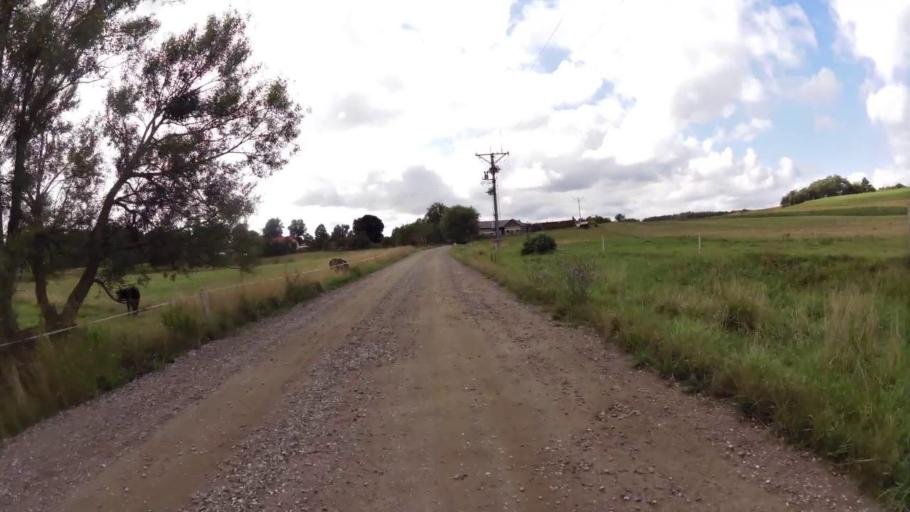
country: PL
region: West Pomeranian Voivodeship
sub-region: Powiat mysliborski
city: Debno
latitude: 52.7916
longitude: 14.6967
